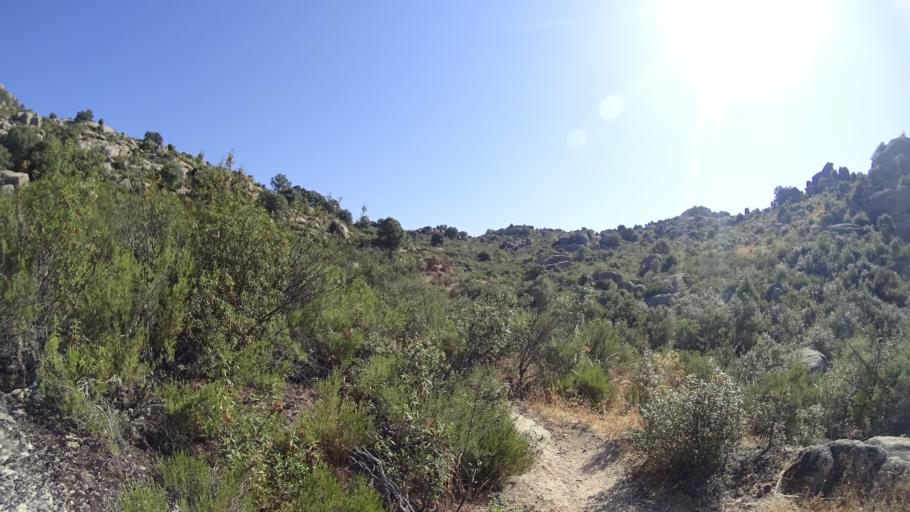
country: ES
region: Madrid
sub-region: Provincia de Madrid
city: Hoyo de Manzanares
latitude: 40.6447
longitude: -3.9354
